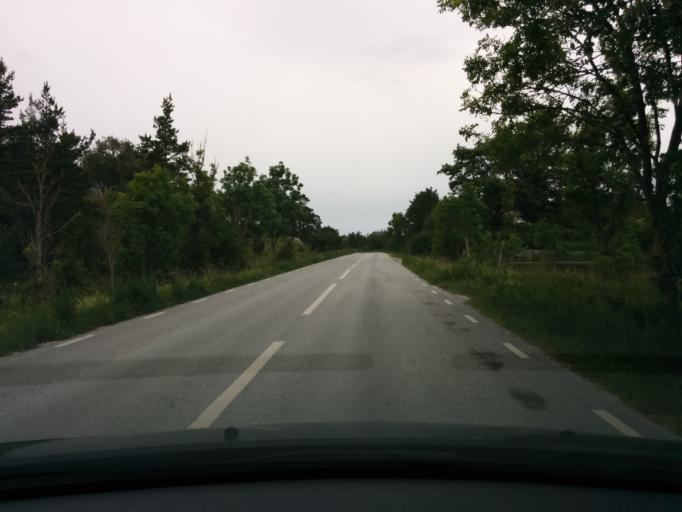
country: SE
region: Gotland
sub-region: Gotland
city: Slite
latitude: 57.6686
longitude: 18.7750
